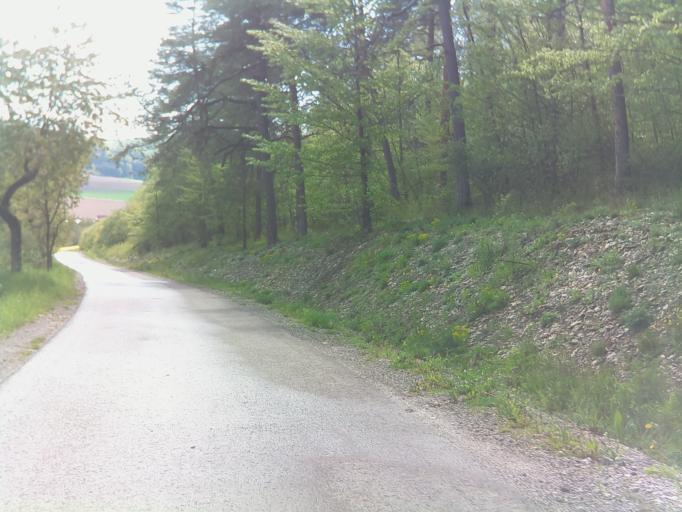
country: DE
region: Thuringia
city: Beinerstadt
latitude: 50.4636
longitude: 10.5522
